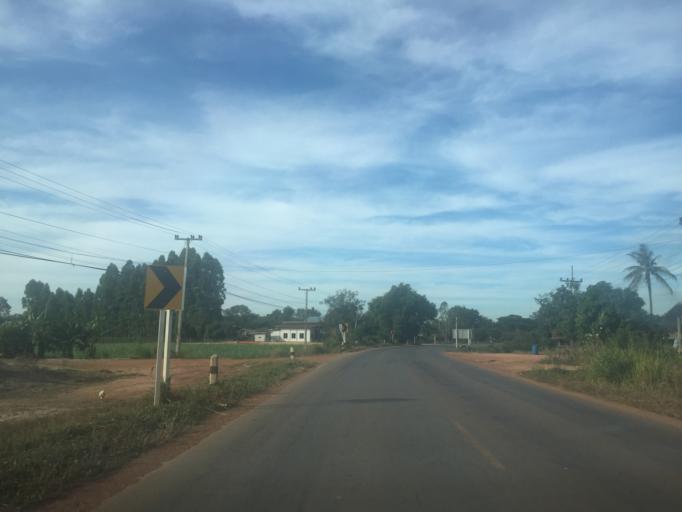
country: TH
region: Changwat Udon Thani
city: Si That
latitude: 16.9881
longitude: 103.1659
